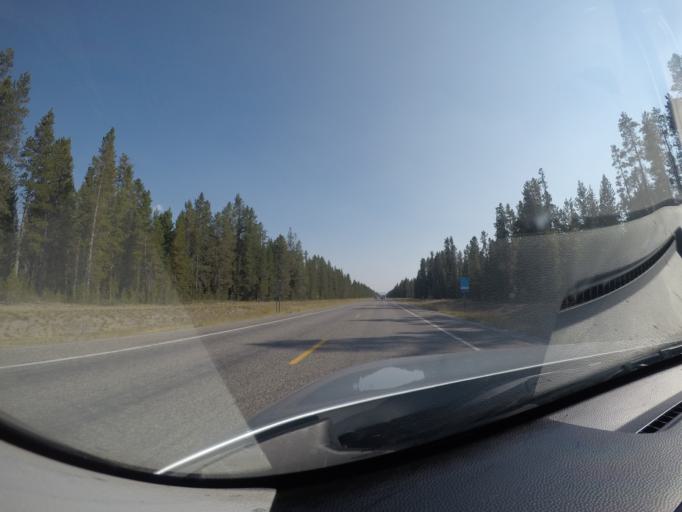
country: US
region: Montana
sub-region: Gallatin County
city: West Yellowstone
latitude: 44.7622
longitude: -111.1134
